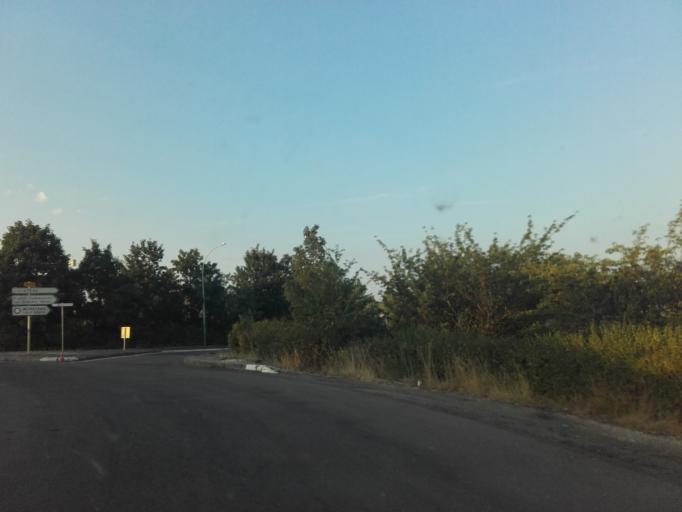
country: FR
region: Bourgogne
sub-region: Departement de l'Yonne
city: Gurgy
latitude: 47.8492
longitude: 3.5497
